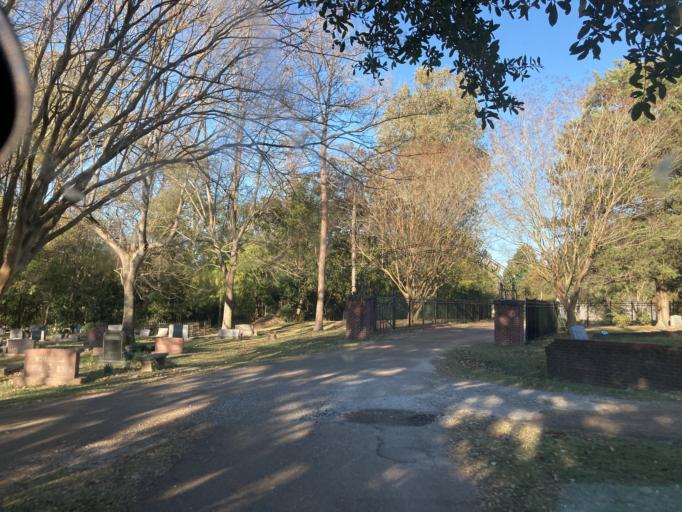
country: US
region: Mississippi
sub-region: Yazoo County
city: Yazoo City
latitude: 32.8512
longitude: -90.4017
